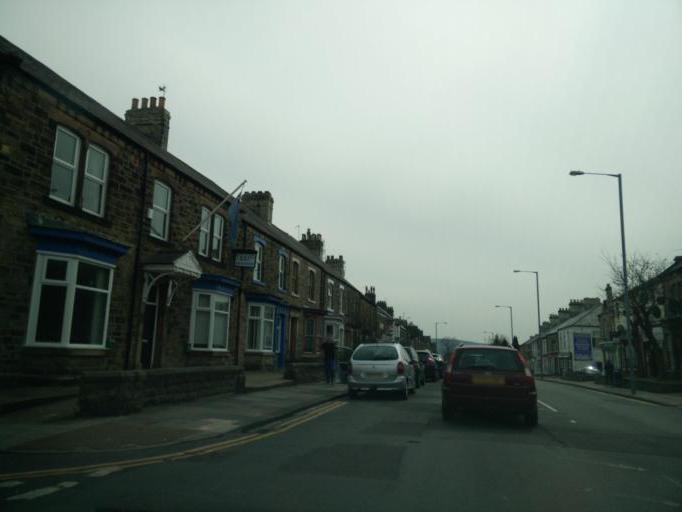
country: GB
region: England
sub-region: County Durham
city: Bishop Auckland
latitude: 54.6543
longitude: -1.6775
